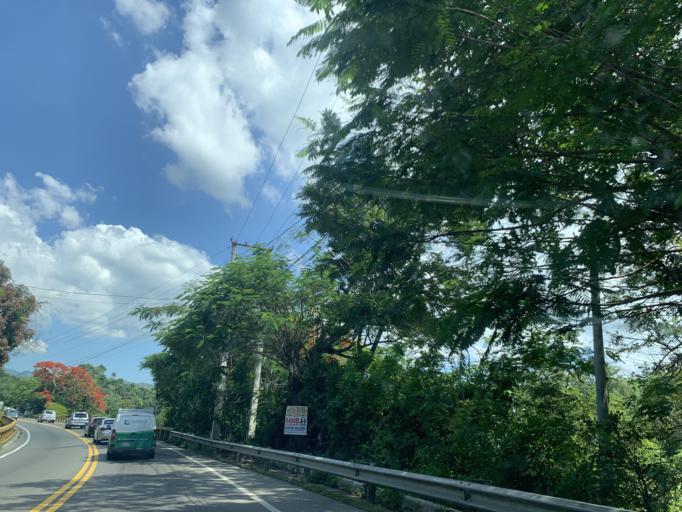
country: DO
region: Puerto Plata
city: Altamira
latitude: 19.6848
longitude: -70.8408
